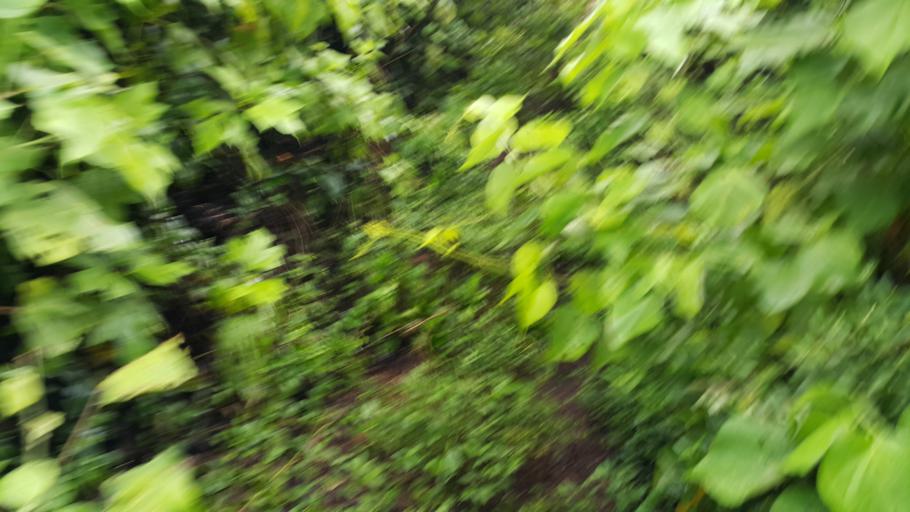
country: NI
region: Chinandega
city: Jiquilillo
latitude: 12.9745
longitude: -87.5529
